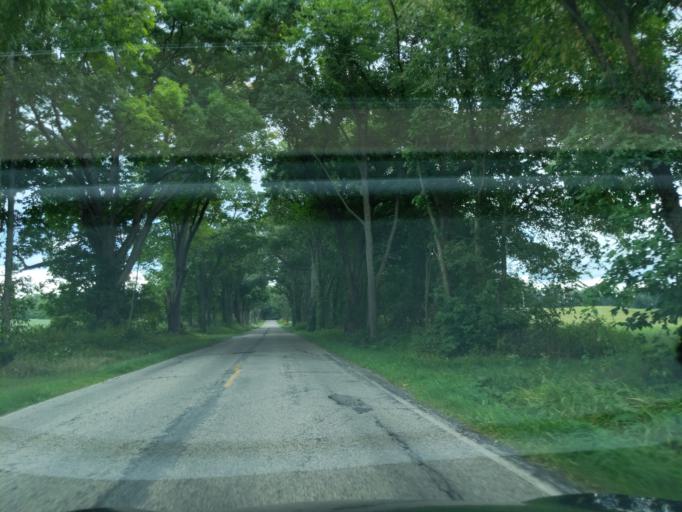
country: US
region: Michigan
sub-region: Eaton County
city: Eaton Rapids
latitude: 42.3787
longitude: -84.5956
